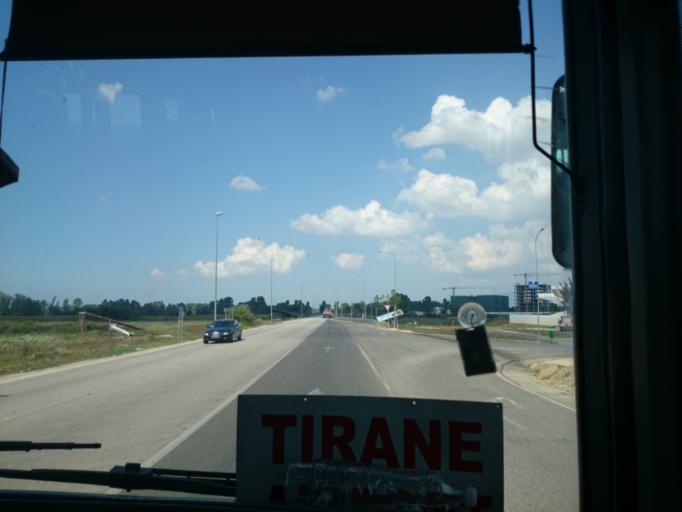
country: AL
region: Tirane
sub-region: Rrethi i Tiranes
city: Berxull
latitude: 41.4039
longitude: 19.7042
